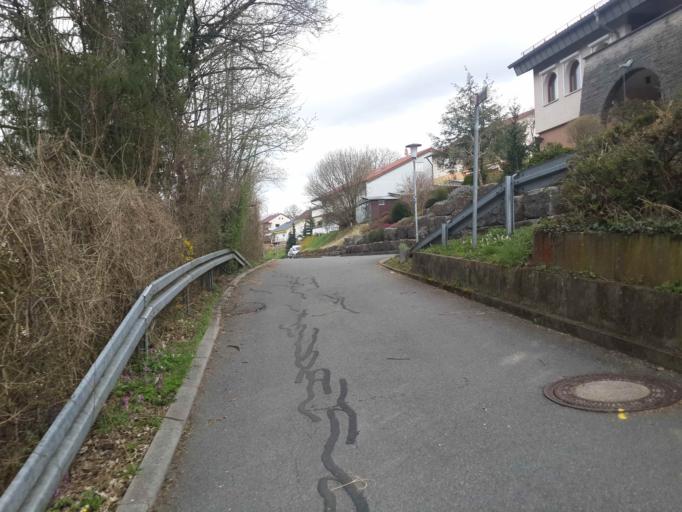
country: DE
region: Baden-Wuerttemberg
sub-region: Karlsruhe Region
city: Billigheim
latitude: 49.3446
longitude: 9.2558
